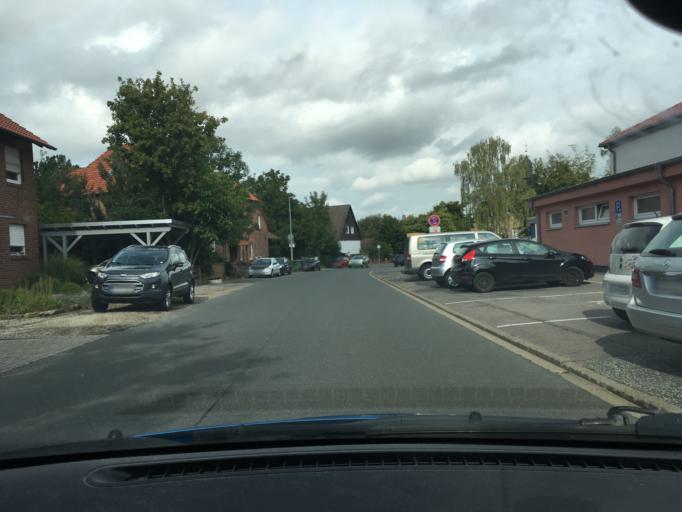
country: DE
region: Lower Saxony
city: Egestorf
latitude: 52.2873
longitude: 9.5091
